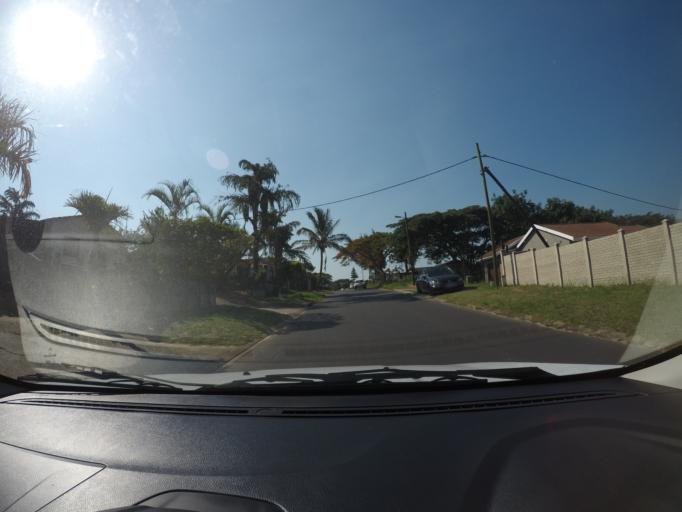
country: ZA
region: KwaZulu-Natal
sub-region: uThungulu District Municipality
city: Richards Bay
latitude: -28.7182
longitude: 32.0435
